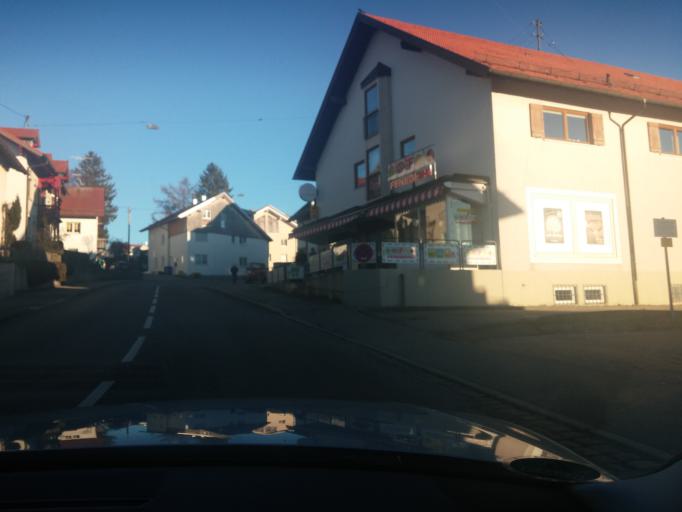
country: DE
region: Bavaria
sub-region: Swabia
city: Altusried
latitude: 47.8037
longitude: 10.2152
